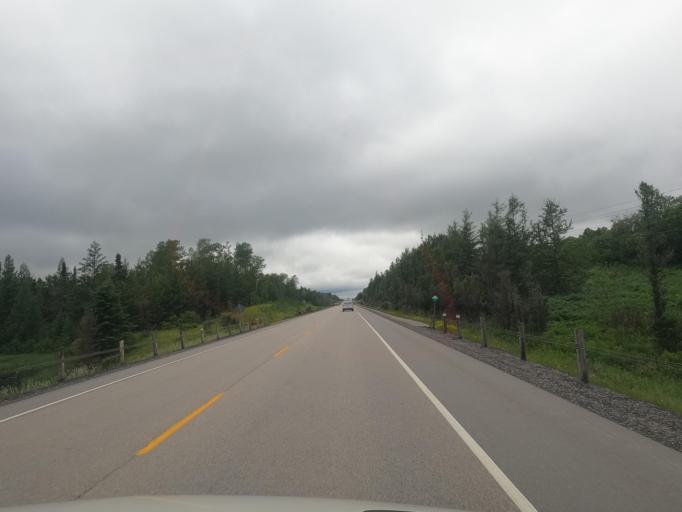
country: CA
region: Ontario
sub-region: Rainy River District
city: Atikokan
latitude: 49.0509
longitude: -90.4960
